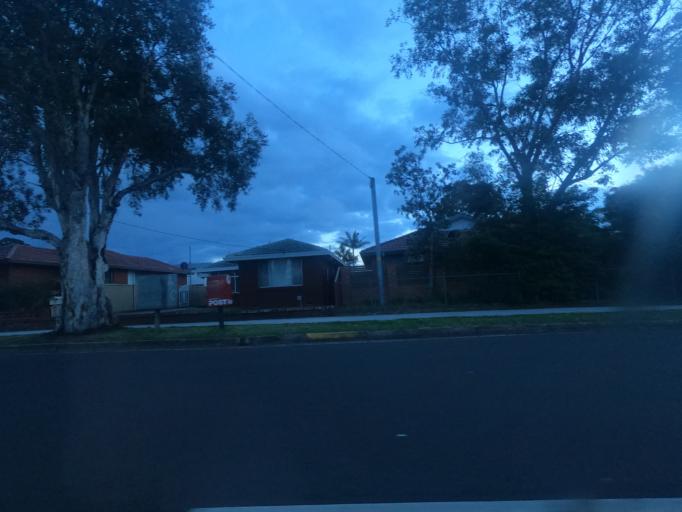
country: AU
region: New South Wales
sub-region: Wollongong
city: Koonawarra
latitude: -34.4990
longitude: 150.8029
